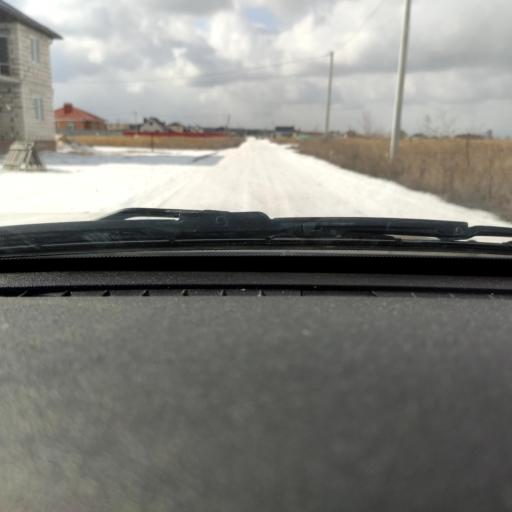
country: RU
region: Voronezj
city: Novaya Usman'
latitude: 51.6606
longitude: 39.4609
